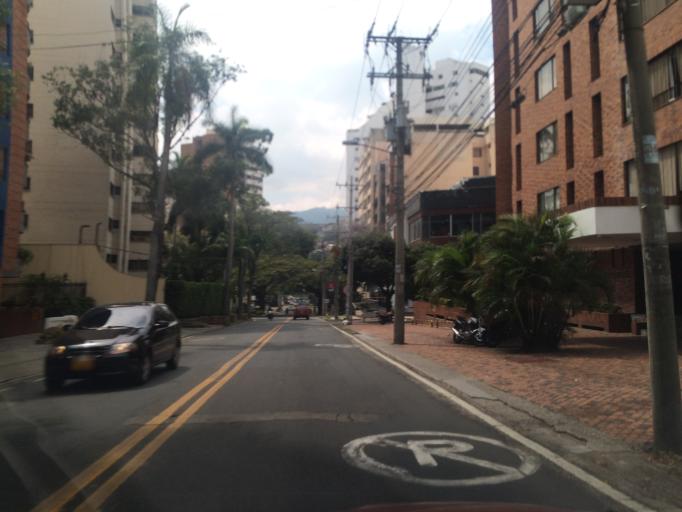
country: CO
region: Valle del Cauca
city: Cali
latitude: 3.4515
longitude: -76.5474
